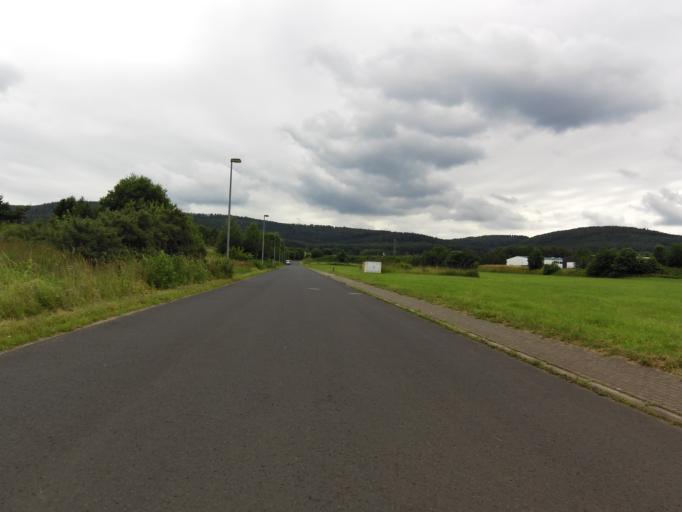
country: DE
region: Thuringia
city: Stadtlengsfeld
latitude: 50.8194
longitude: 10.1349
